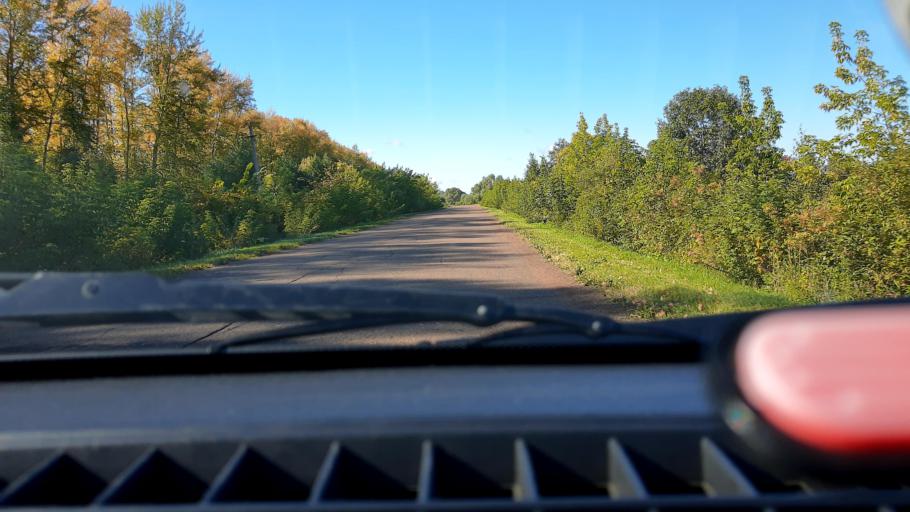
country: RU
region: Bashkortostan
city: Kushnarenkovo
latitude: 55.1093
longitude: 55.5282
